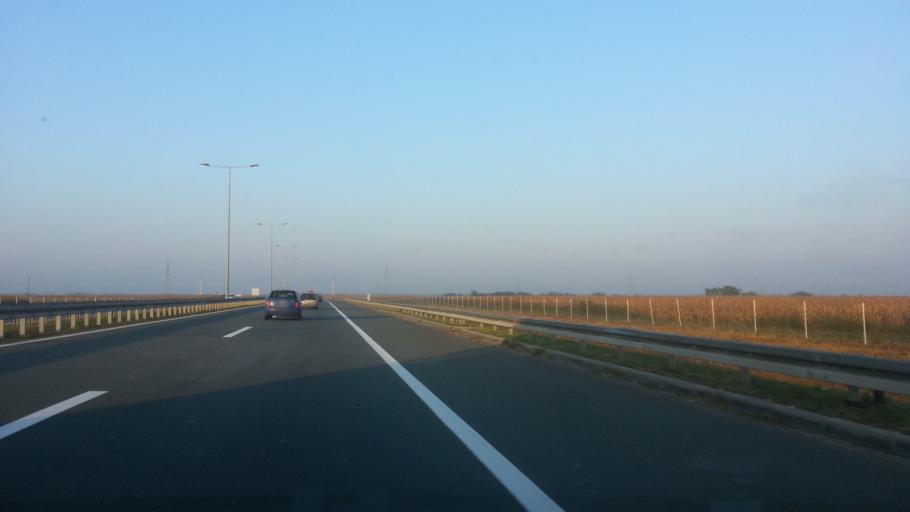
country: RS
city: Novi Banovci
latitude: 44.8846
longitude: 20.2802
